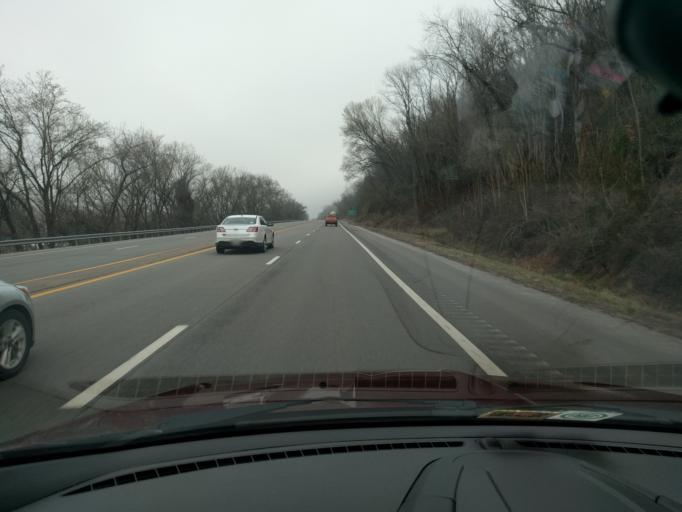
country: US
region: West Virginia
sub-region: Kanawha County
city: Marmet
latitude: 38.2632
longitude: -81.5649
